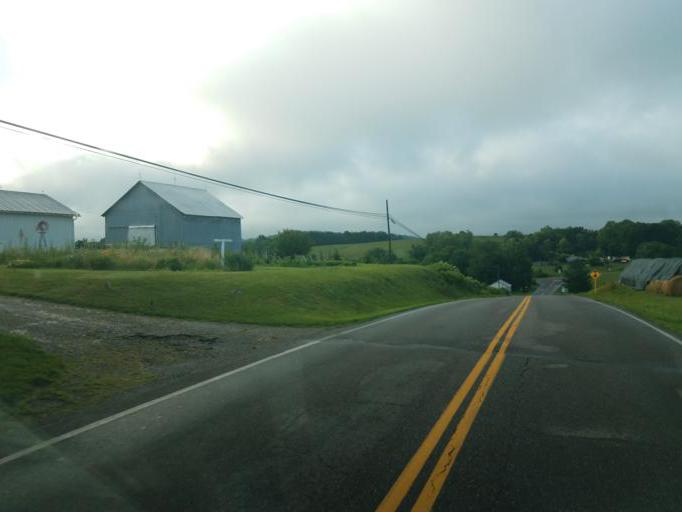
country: US
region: Ohio
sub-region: Gallia County
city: Gallipolis
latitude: 38.7982
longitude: -82.3997
